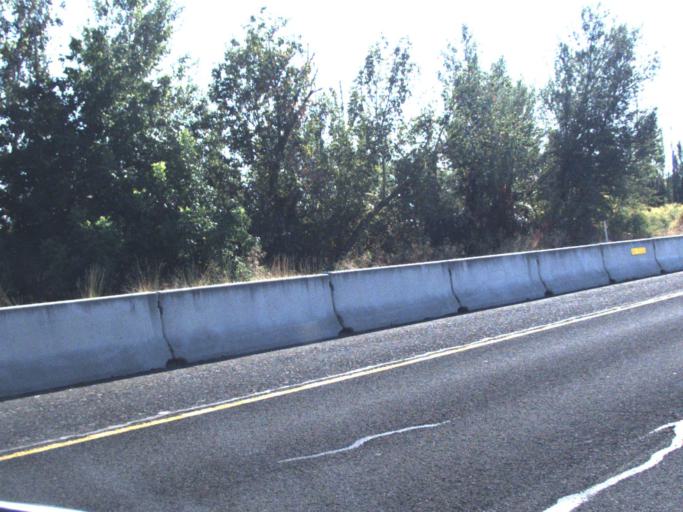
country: US
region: Washington
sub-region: Walla Walla County
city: College Place
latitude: 46.0426
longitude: -118.3611
